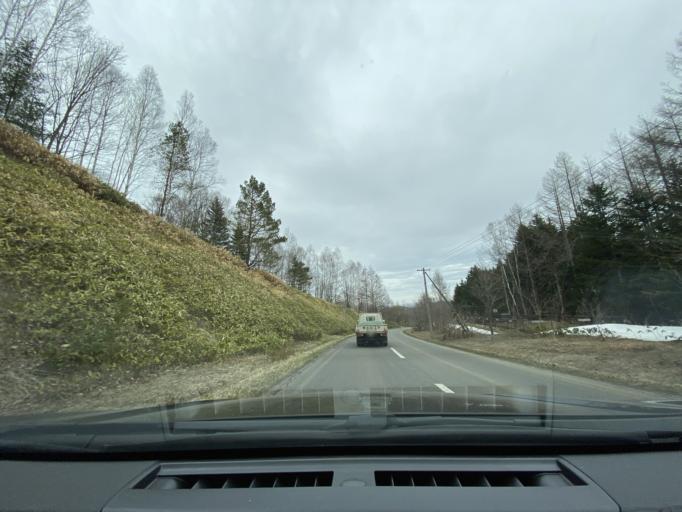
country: JP
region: Hokkaido
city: Nayoro
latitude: 44.0927
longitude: 142.4644
